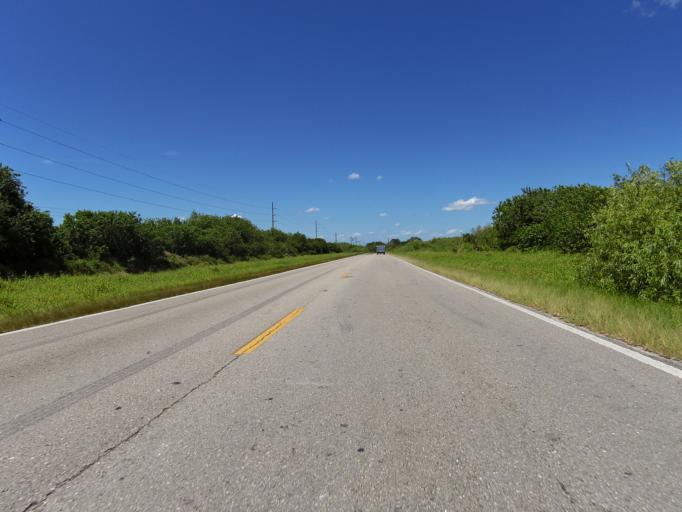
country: US
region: Florida
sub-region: Collier County
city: Immokalee
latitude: 26.3627
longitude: -81.4167
